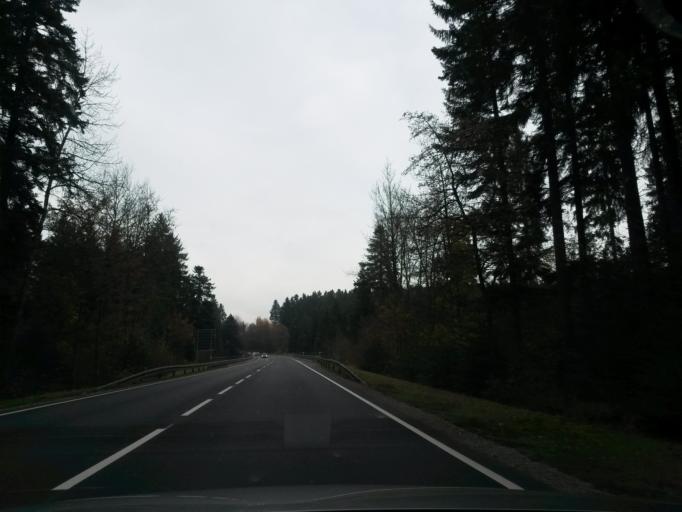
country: DE
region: Baden-Wuerttemberg
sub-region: Karlsruhe Region
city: Freudenstadt
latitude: 48.4517
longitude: 8.4409
